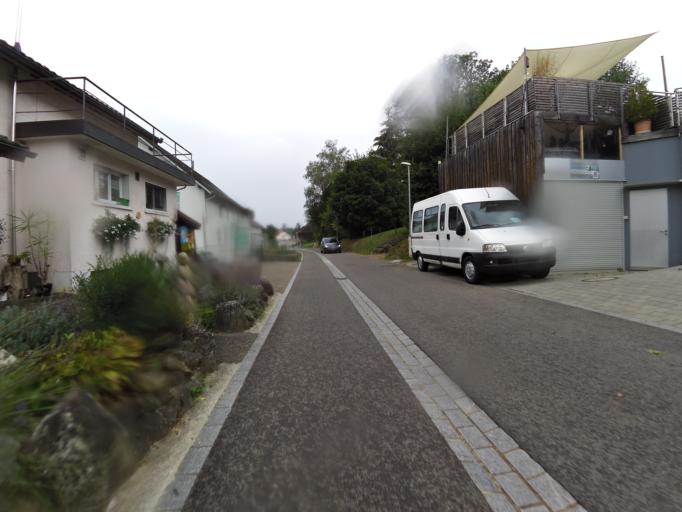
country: CH
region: Thurgau
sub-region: Weinfelden District
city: Wigoltingen
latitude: 47.6022
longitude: 9.0317
